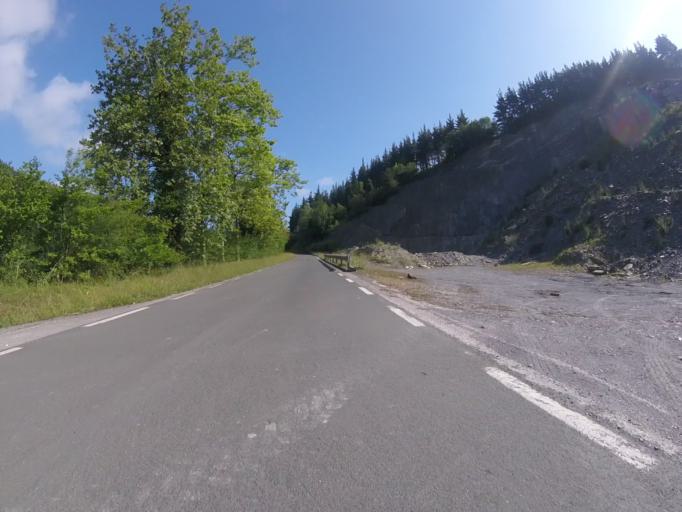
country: ES
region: Basque Country
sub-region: Provincia de Guipuzcoa
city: Ormaiztegui
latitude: 43.0667
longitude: -2.2378
